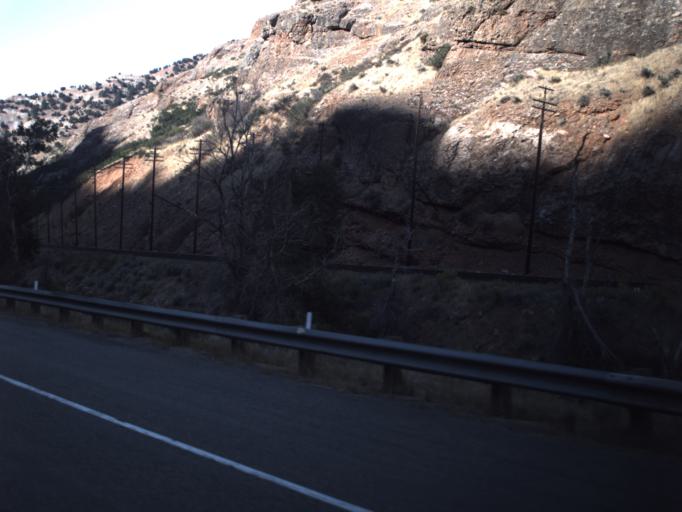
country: US
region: Utah
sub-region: Morgan County
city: Morgan
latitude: 41.0482
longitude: -111.5271
